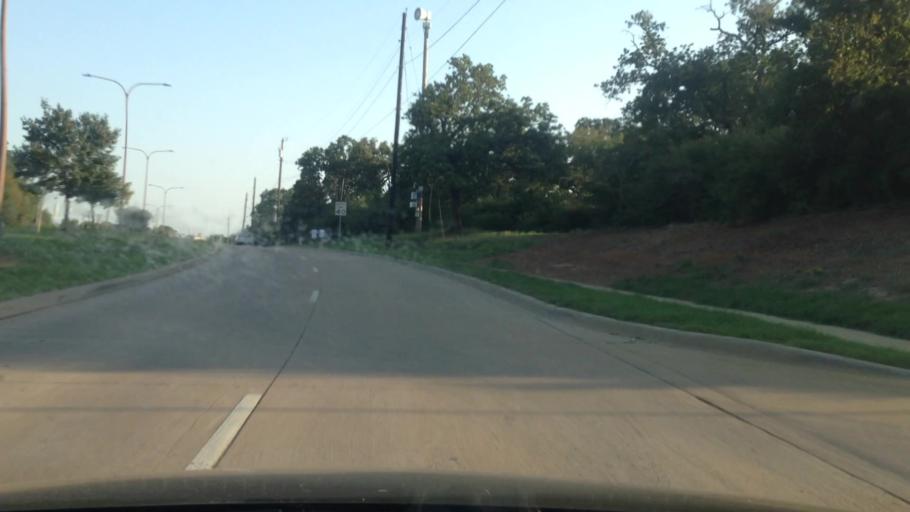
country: US
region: Texas
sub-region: Tarrant County
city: Dalworthington Gardens
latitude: 32.6802
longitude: -97.1669
